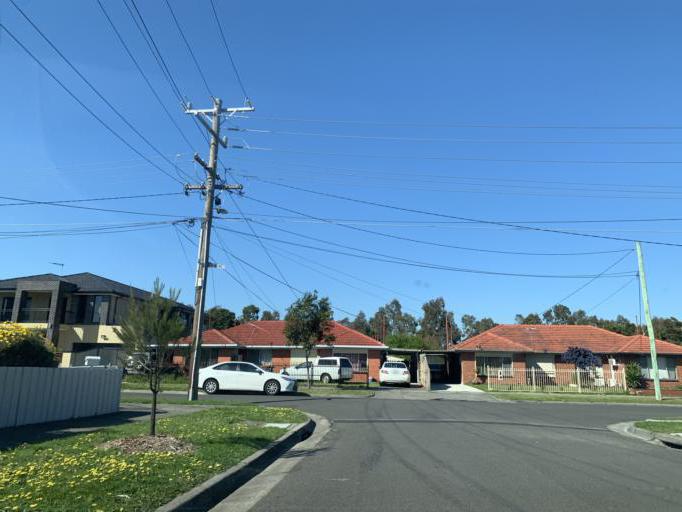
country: AU
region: Victoria
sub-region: Greater Dandenong
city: Dandenong
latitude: -38.0016
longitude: 145.2056
